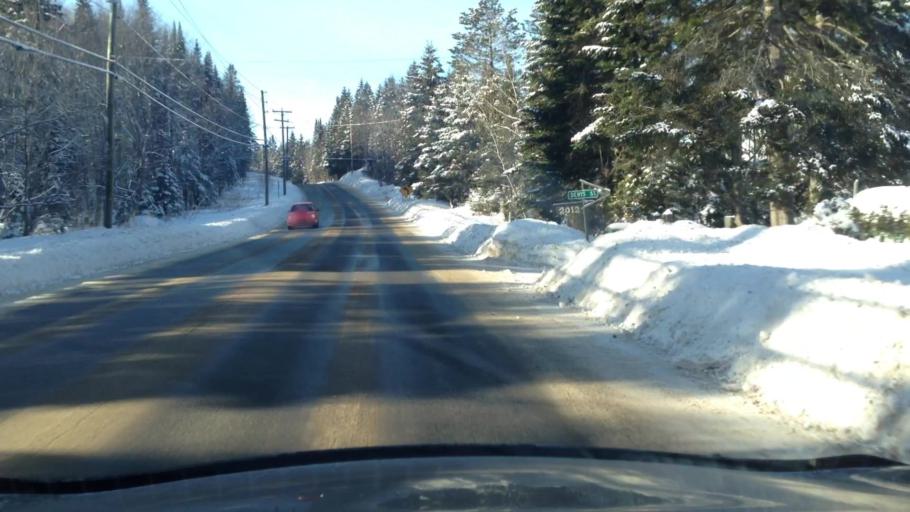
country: CA
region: Quebec
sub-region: Laurentides
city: Sainte-Agathe-des-Monts
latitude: 45.9287
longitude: -74.4051
